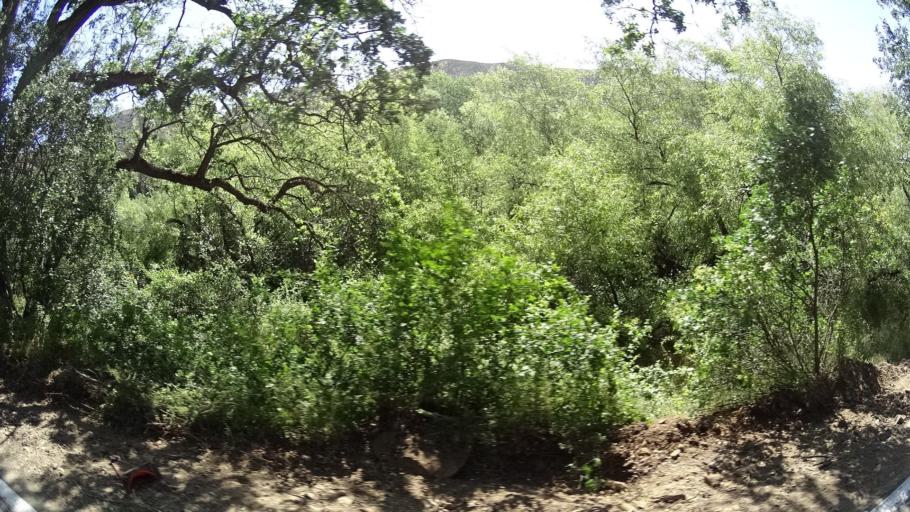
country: US
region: California
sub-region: Lake County
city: Clearlake
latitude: 39.0382
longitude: -122.5732
